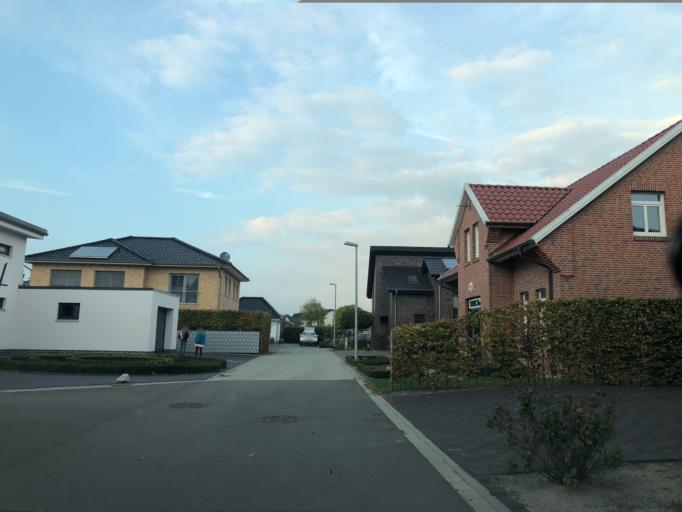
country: DE
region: Lower Saxony
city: Papenburg
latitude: 53.0723
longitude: 7.4545
